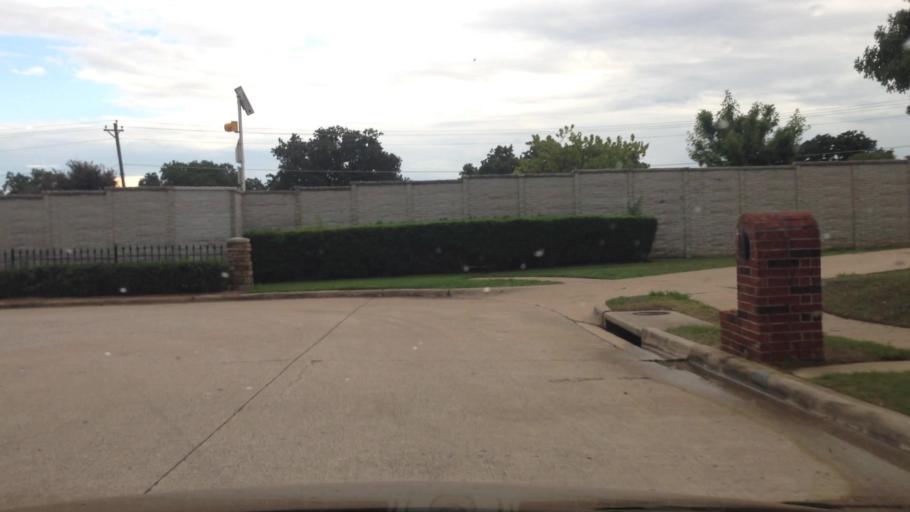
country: US
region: Texas
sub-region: Denton County
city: Flower Mound
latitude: 33.0143
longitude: -97.0526
